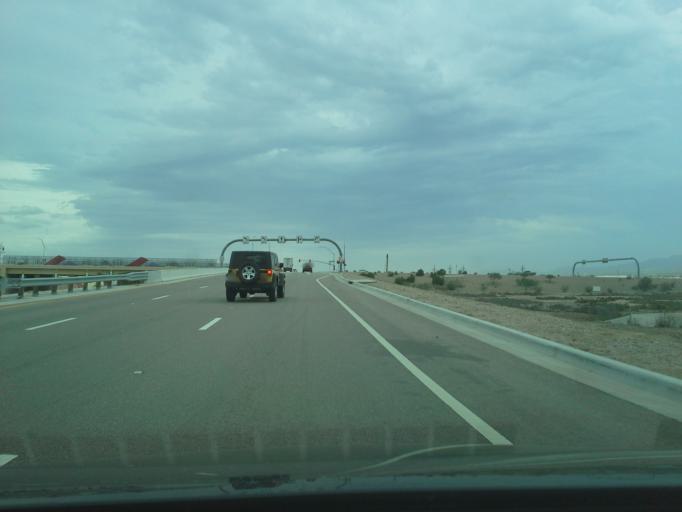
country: US
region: Arizona
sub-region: Pima County
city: Tortolita
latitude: 32.3806
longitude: -111.1117
